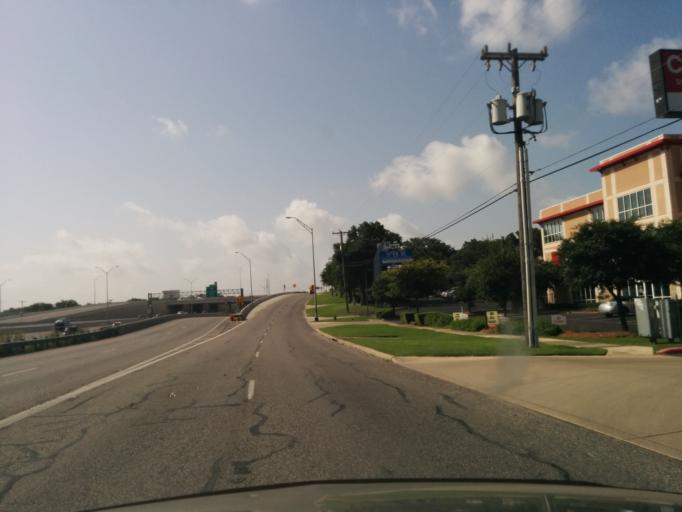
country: US
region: Texas
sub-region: Bexar County
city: Balcones Heights
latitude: 29.5258
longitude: -98.5575
